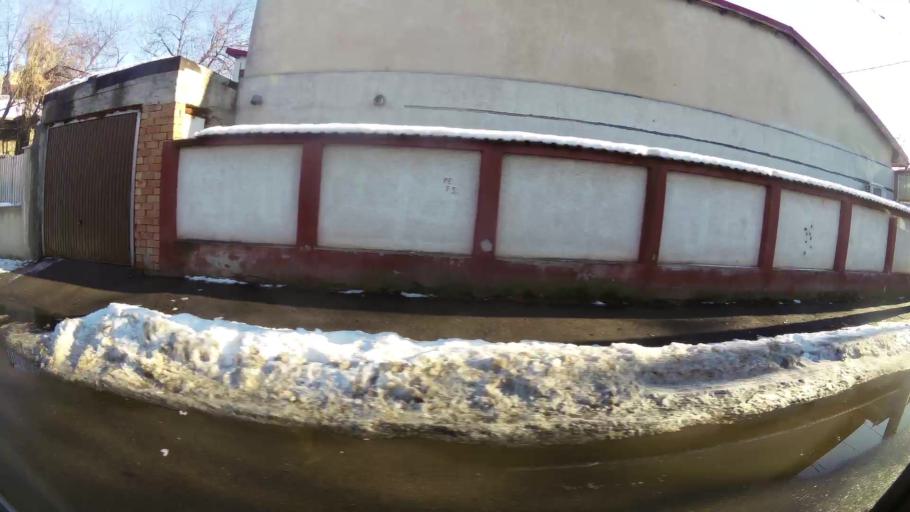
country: RO
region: Bucuresti
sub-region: Municipiul Bucuresti
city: Bucuresti
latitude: 44.3918
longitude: 26.0894
